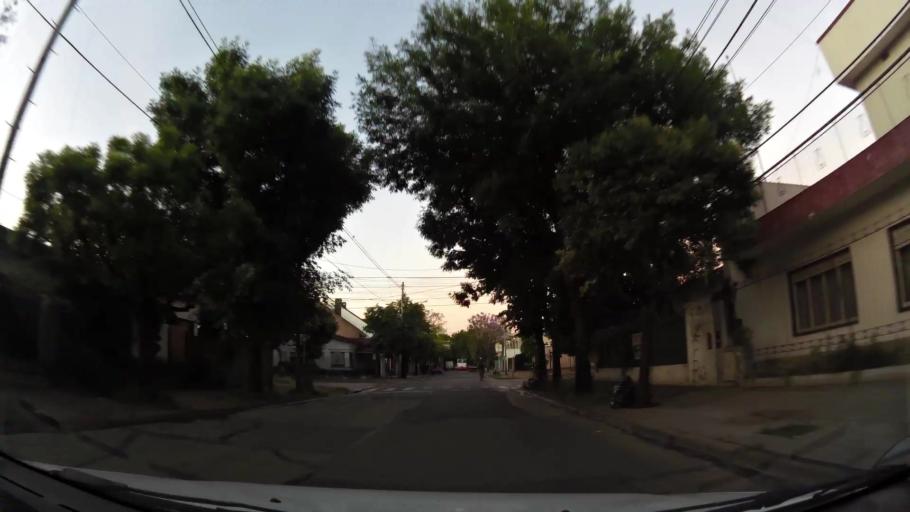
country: AR
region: Buenos Aires
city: Ituzaingo
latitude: -34.6568
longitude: -58.6421
